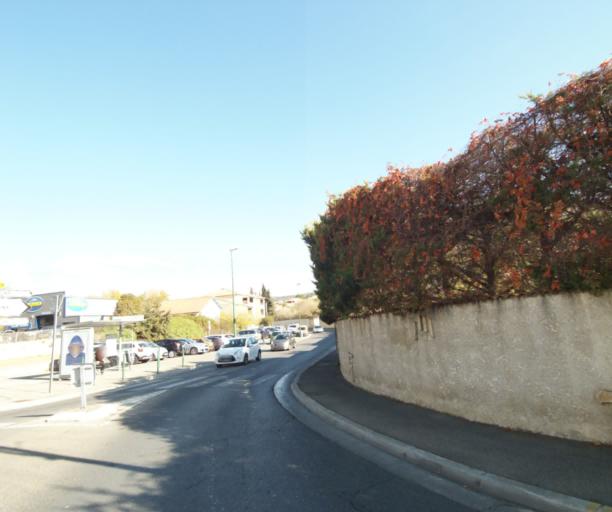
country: FR
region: Provence-Alpes-Cote d'Azur
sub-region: Departement des Bouches-du-Rhone
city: Allauch
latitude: 43.3543
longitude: 5.4849
